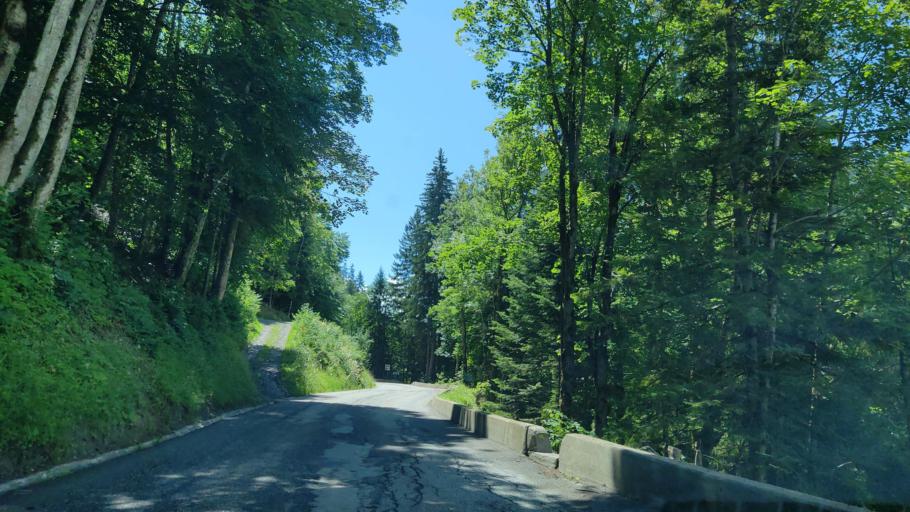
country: FR
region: Rhone-Alpes
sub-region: Departement de la Haute-Savoie
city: Praz-sur-Arly
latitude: 45.8377
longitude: 6.5081
